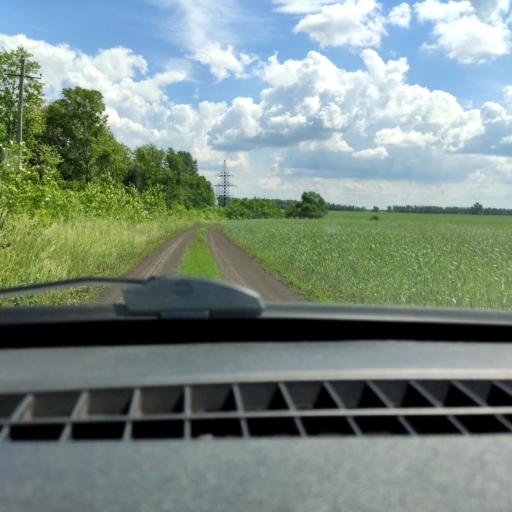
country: RU
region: Bashkortostan
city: Kabakovo
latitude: 54.5235
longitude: 56.0669
